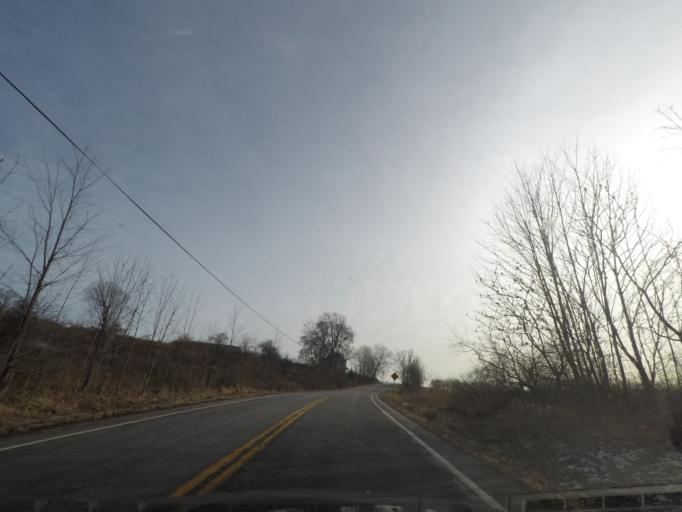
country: US
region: New York
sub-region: Saratoga County
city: Stillwater
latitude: 42.9894
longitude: -73.6991
